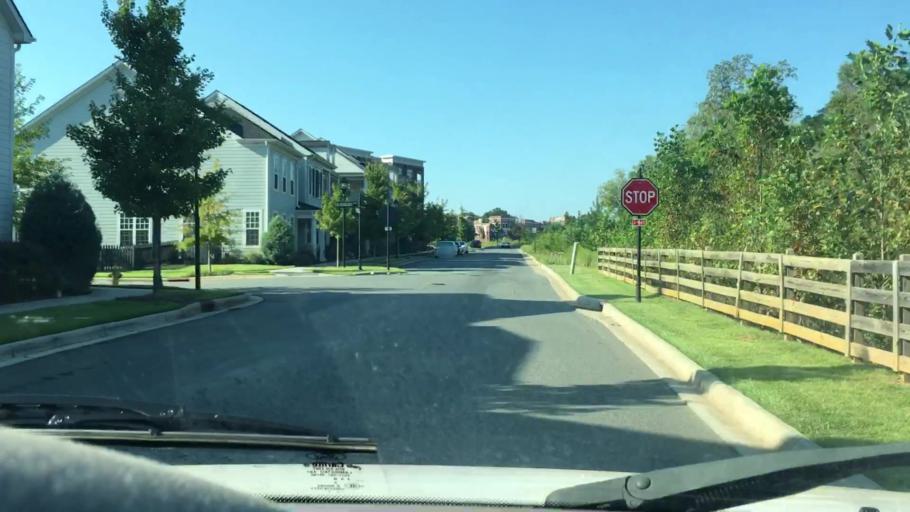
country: US
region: North Carolina
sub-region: Mecklenburg County
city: Cornelius
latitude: 35.4836
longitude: -80.8542
